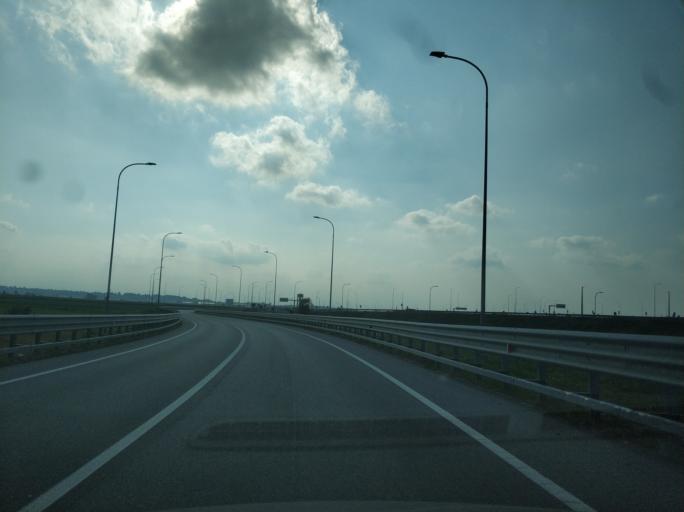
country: IT
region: Piedmont
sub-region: Provincia di Cuneo
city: Roreto
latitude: 44.6634
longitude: 7.8104
